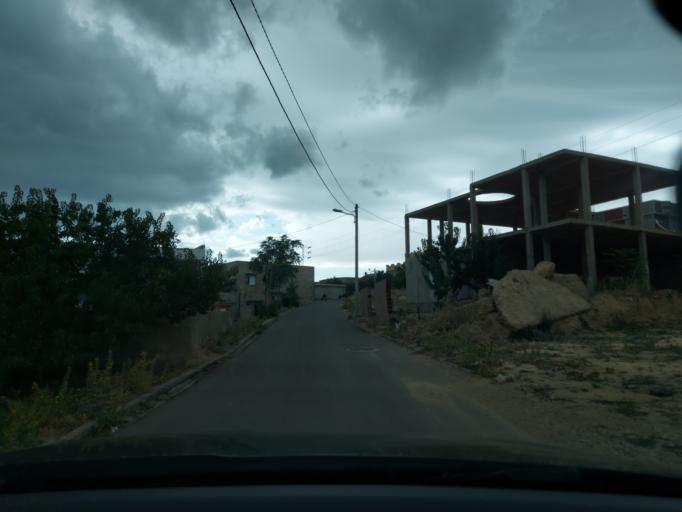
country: TN
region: Silyanah
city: Maktar
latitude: 35.8542
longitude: 9.2000
